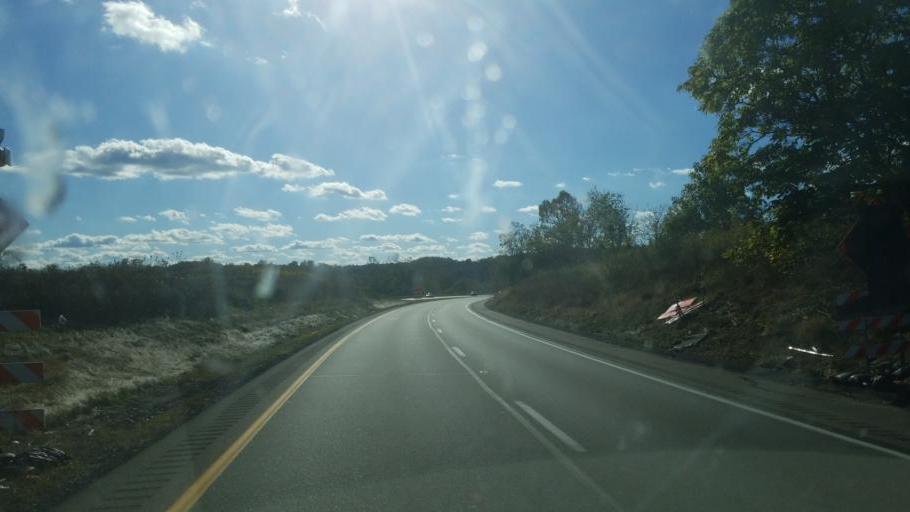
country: US
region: Pennsylvania
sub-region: Washington County
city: Wolfdale
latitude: 40.1314
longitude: -80.3254
